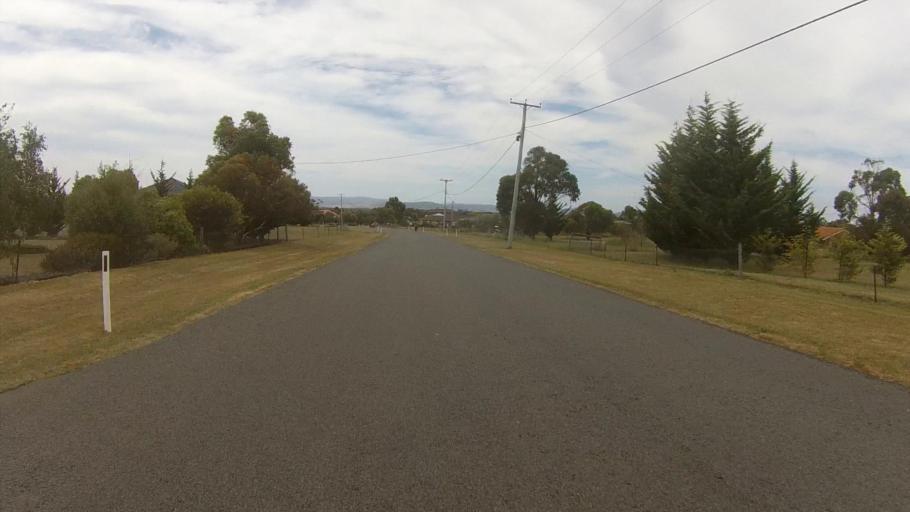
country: AU
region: Tasmania
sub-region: Clarence
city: Cambridge
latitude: -42.8470
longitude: 147.4706
